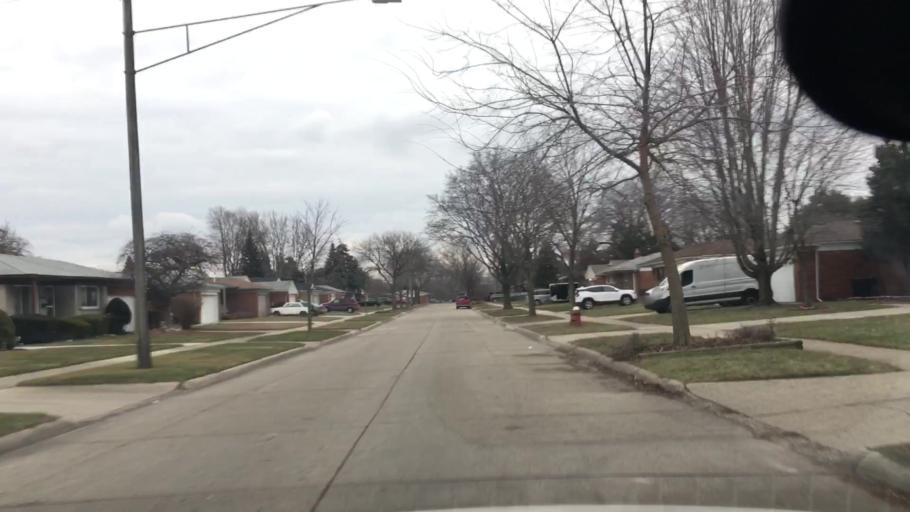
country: US
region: Michigan
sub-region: Oakland County
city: Madison Heights
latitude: 42.4978
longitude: -83.0712
